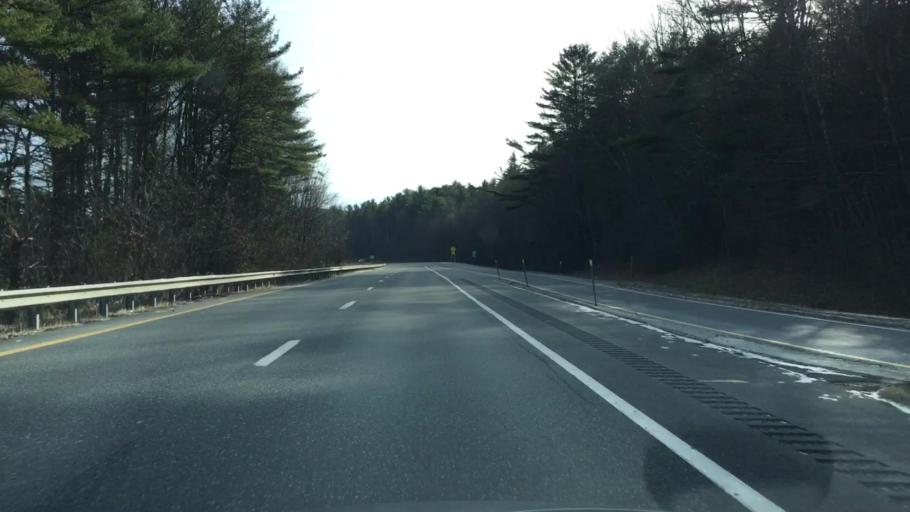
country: US
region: New Hampshire
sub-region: Grafton County
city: Lebanon
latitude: 43.6324
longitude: -72.2111
